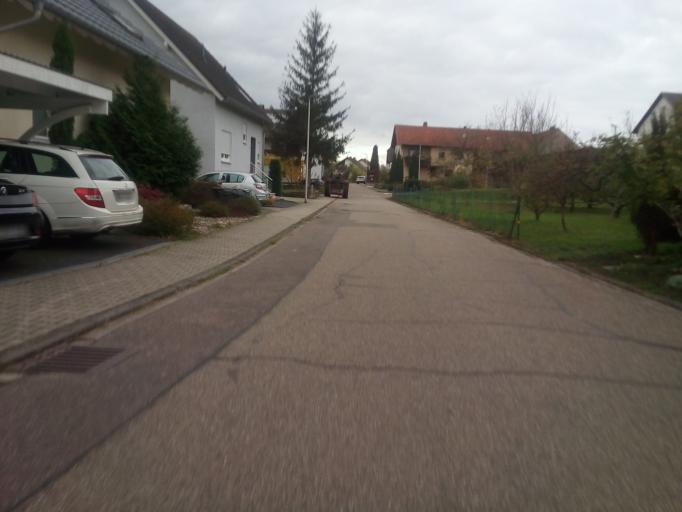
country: DE
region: Baden-Wuerttemberg
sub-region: Karlsruhe Region
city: Schwarzach
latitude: 48.7645
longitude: 8.0467
